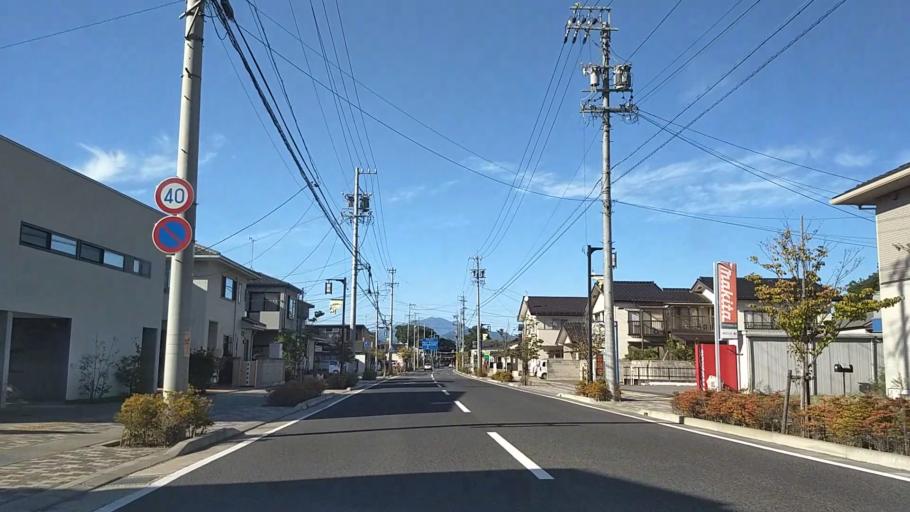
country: JP
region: Nagano
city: Nagano-shi
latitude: 36.5356
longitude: 138.1264
